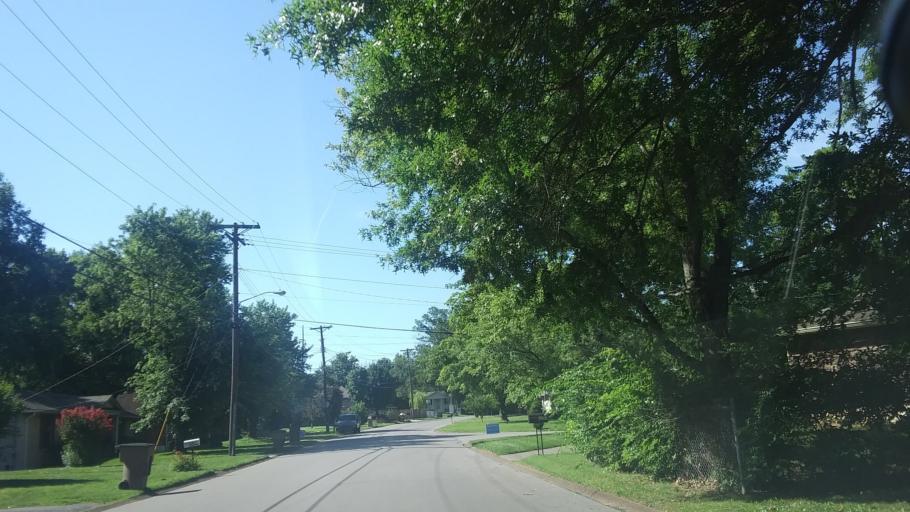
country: US
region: Tennessee
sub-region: Davidson County
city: Oak Hill
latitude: 36.0807
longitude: -86.7093
